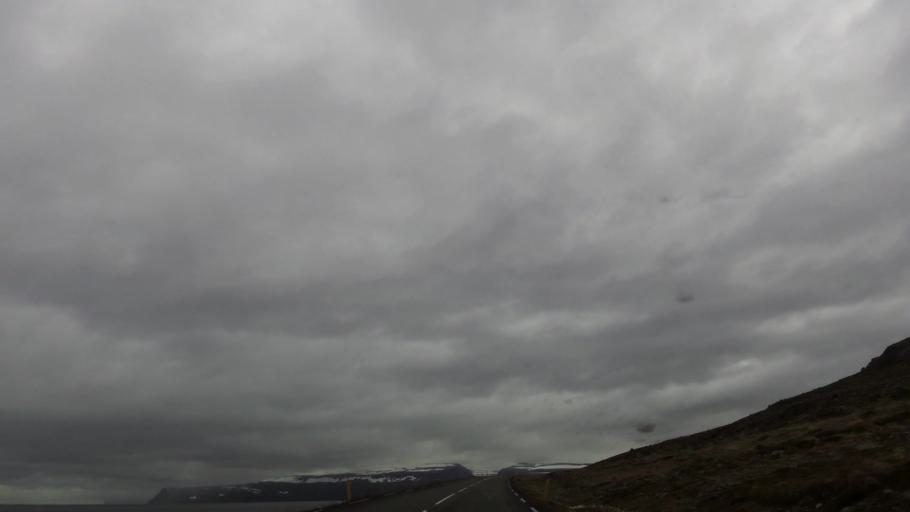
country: IS
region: Westfjords
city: Isafjoerdur
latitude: 66.0442
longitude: -22.7713
